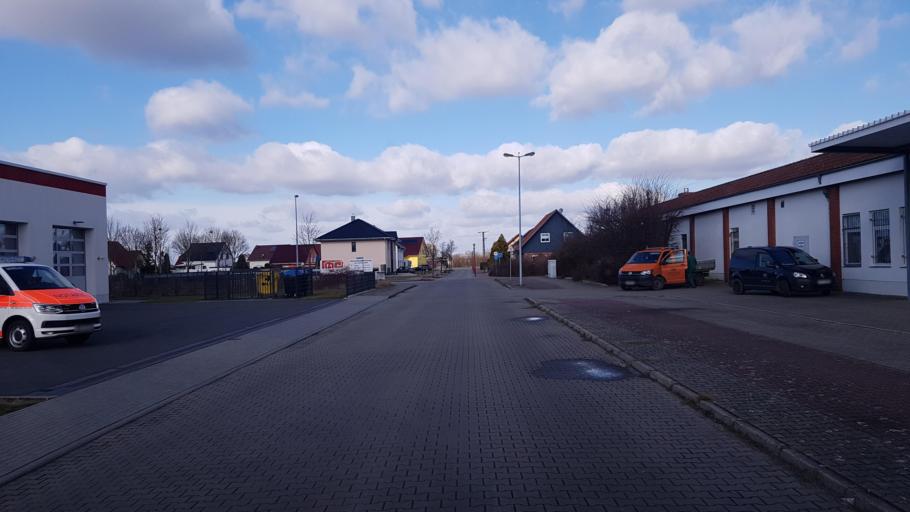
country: DE
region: Brandenburg
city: Herzberg
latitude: 51.6909
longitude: 13.2215
